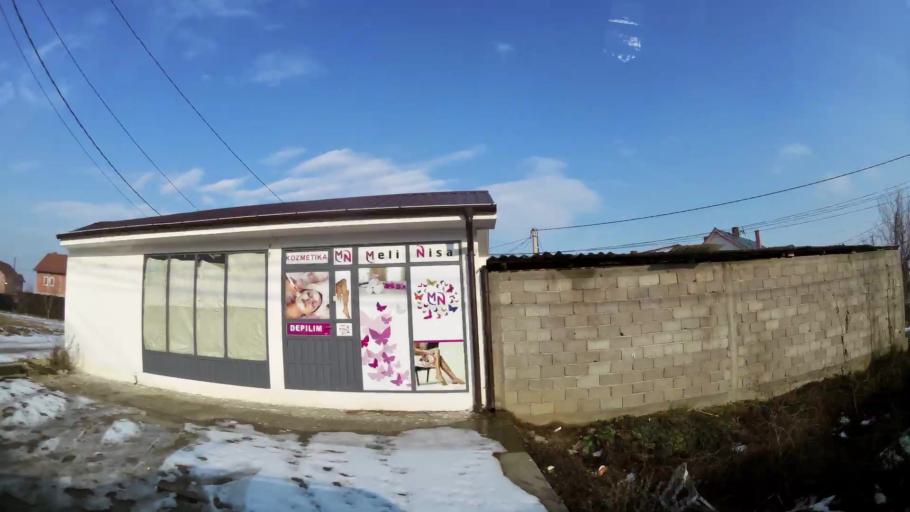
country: MK
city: Creshevo
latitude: 42.0192
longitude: 21.5045
